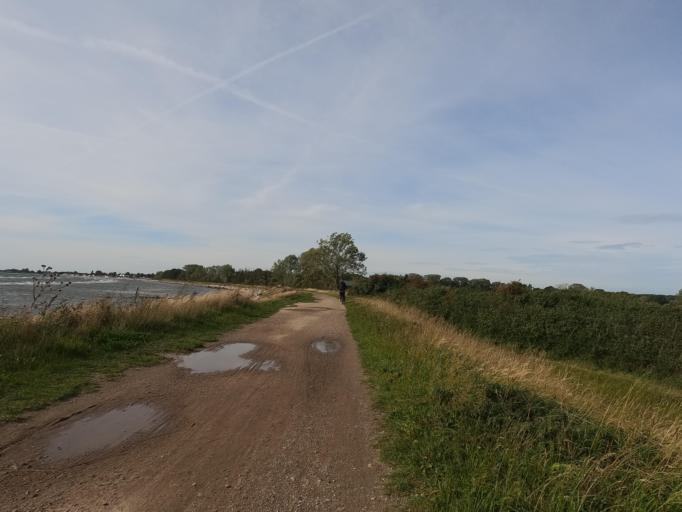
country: DE
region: Schleswig-Holstein
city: Dahme
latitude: 54.1976
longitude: 11.0869
